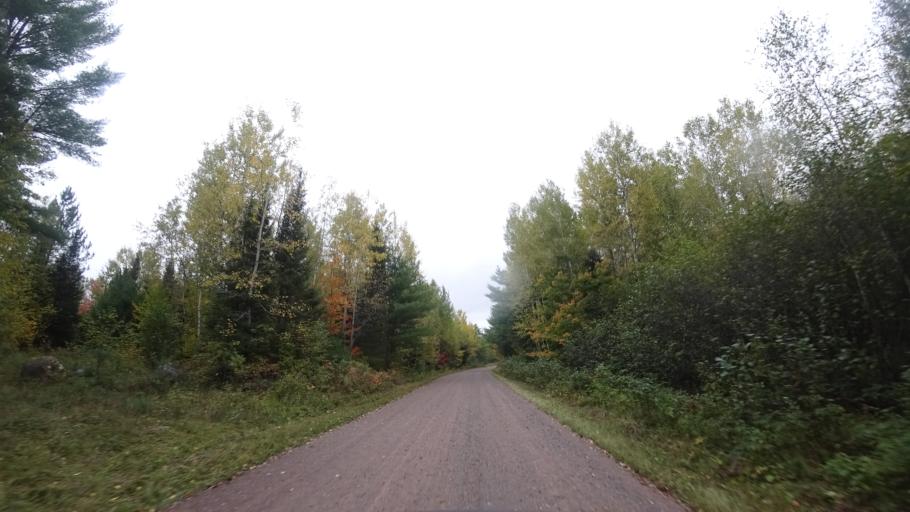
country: US
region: Wisconsin
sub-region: Sawyer County
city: Little Round Lake
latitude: 46.0682
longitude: -90.9943
